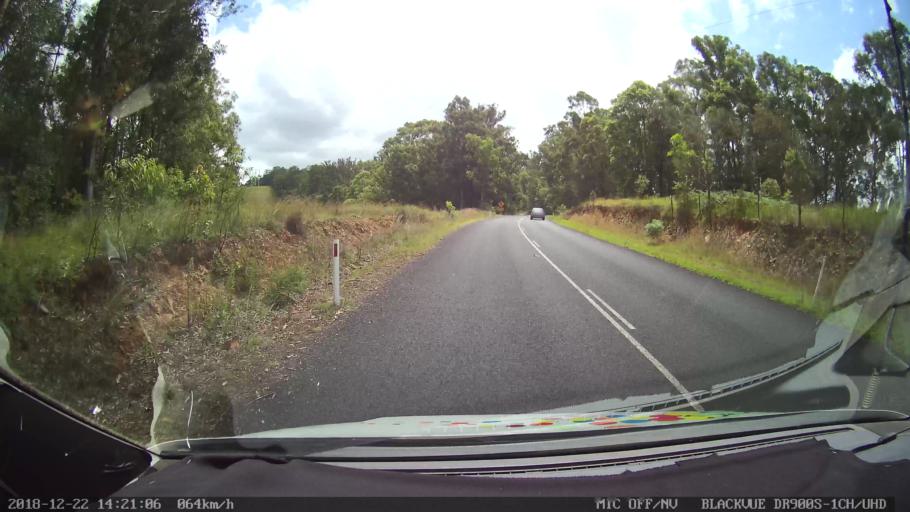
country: AU
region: New South Wales
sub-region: Clarence Valley
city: Coutts Crossing
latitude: -30.0191
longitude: 152.6615
